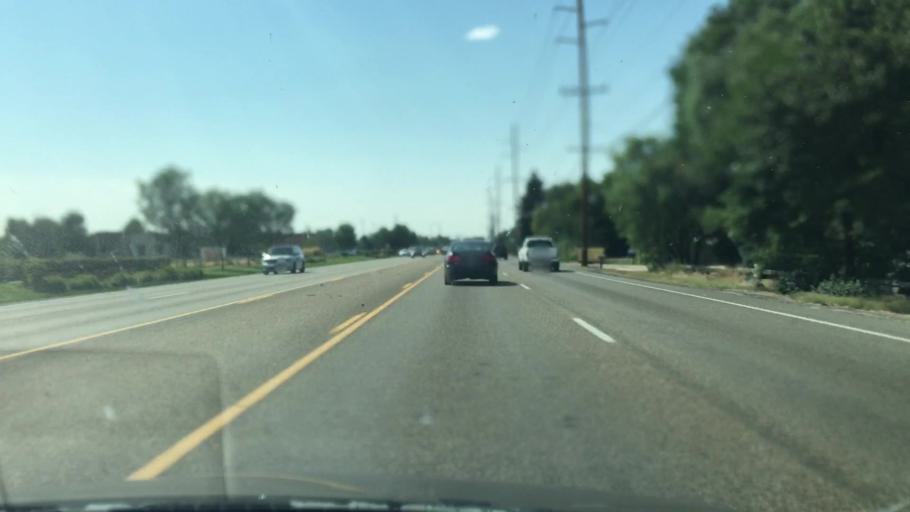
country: US
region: Idaho
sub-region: Ada County
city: Eagle
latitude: 43.6811
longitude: -116.3095
